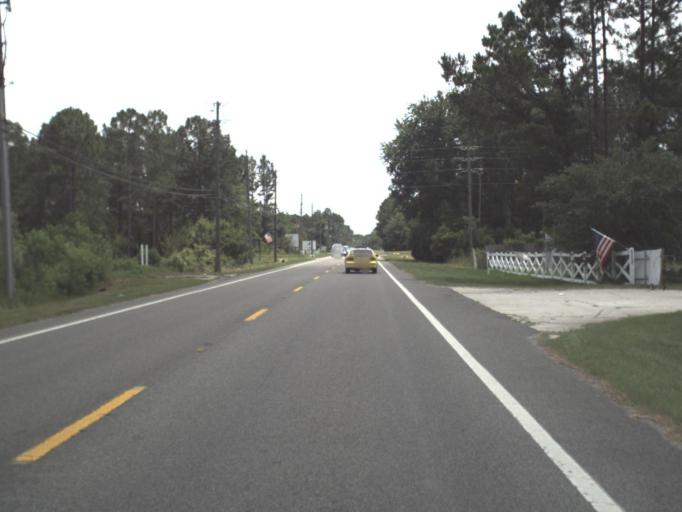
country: US
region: Florida
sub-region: Nassau County
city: Yulee
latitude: 30.6234
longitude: -81.5992
